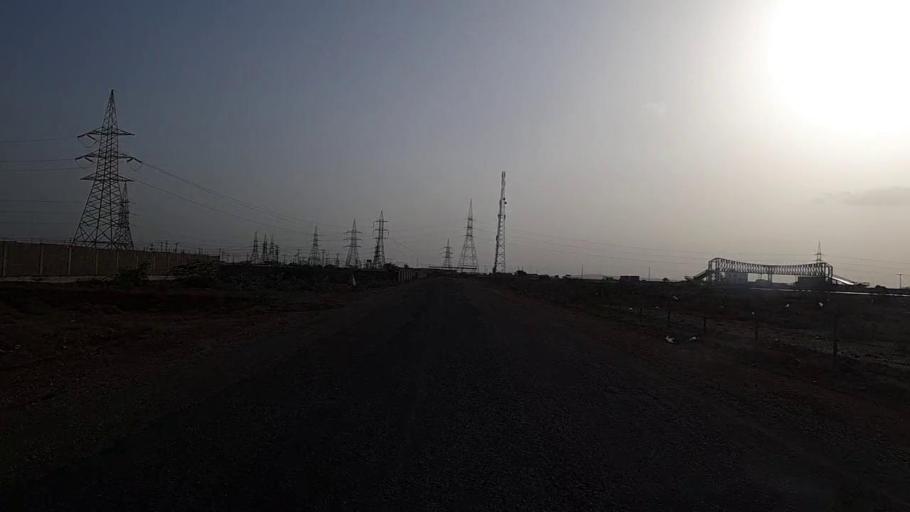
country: PK
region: Sindh
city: Thatta
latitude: 25.1831
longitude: 67.8239
